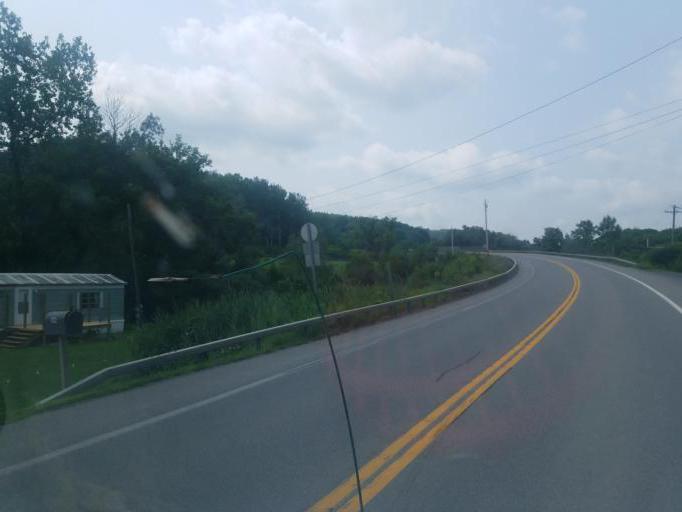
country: US
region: New York
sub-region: Herkimer County
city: Herkimer
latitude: 43.0142
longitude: -74.9226
